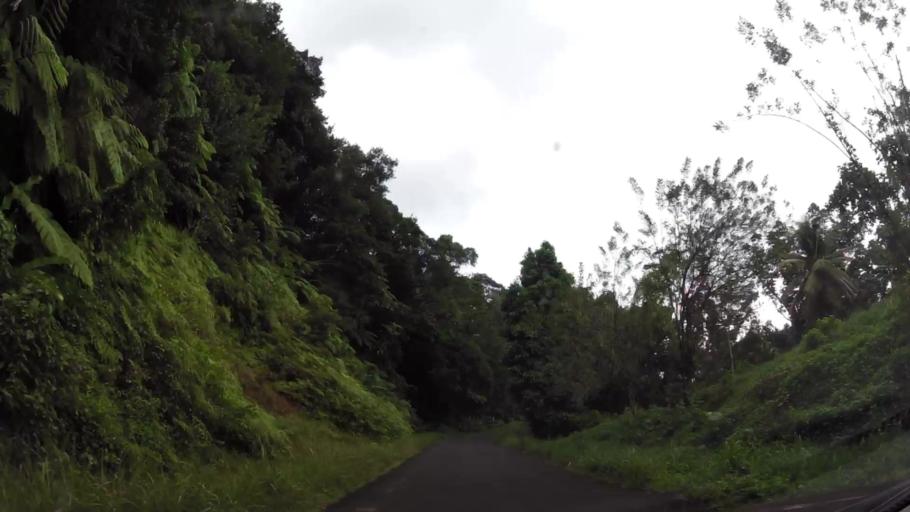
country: DM
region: Saint David
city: Castle Bruce
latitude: 15.4456
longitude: -61.2631
